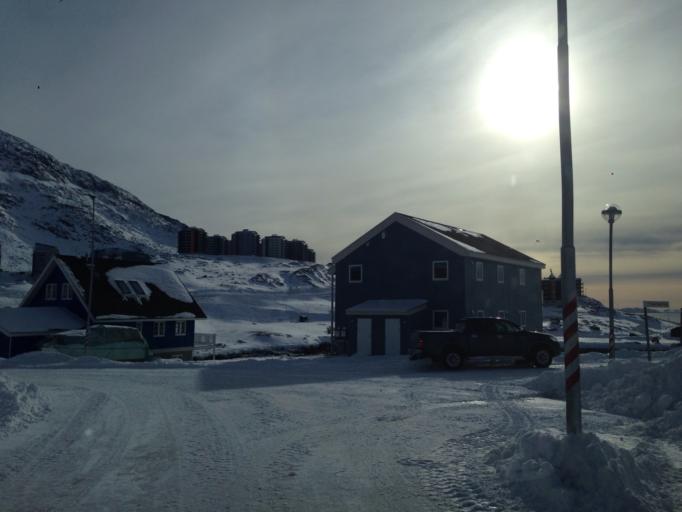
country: GL
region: Sermersooq
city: Nuuk
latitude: 64.1730
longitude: -51.6737
